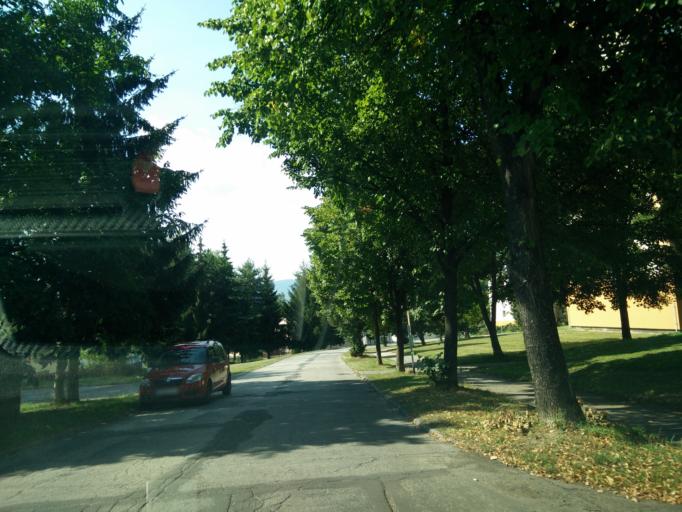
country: SK
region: Nitriansky
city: Prievidza
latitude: 48.7776
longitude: 18.6413
